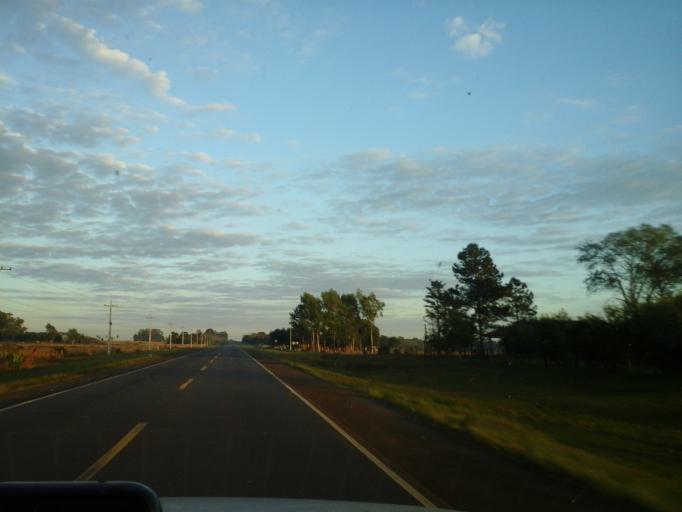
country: PY
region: Misiones
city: San Patricio
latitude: -27.0348
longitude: -56.6753
